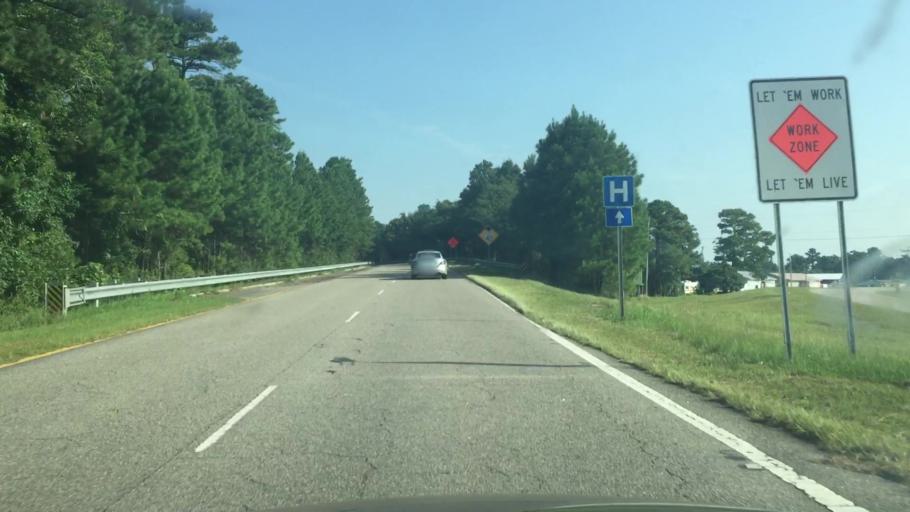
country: US
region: South Carolina
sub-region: Horry County
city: Little River
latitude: 33.8608
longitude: -78.6567
